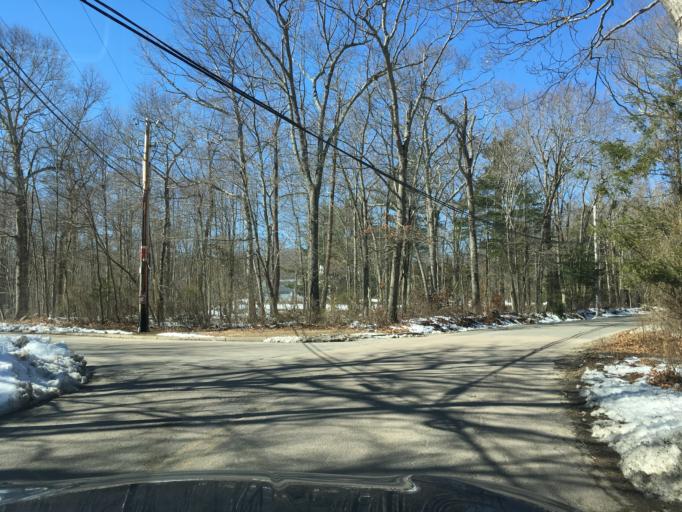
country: US
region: Rhode Island
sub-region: Washington County
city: Exeter
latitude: 41.6067
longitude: -71.5342
